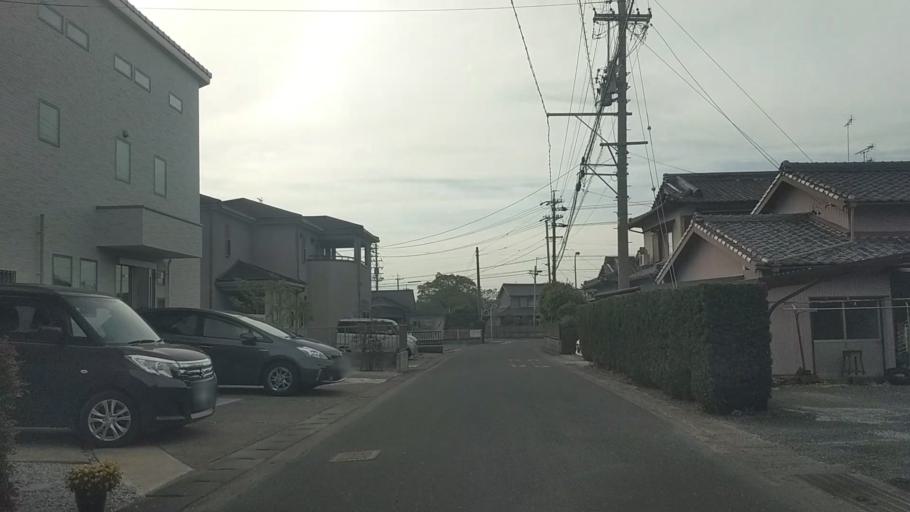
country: JP
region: Shizuoka
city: Kosai-shi
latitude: 34.7591
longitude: 137.6117
